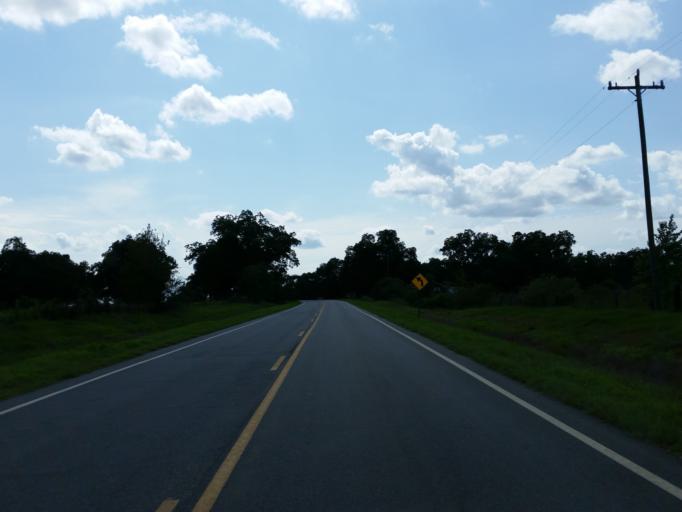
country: US
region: Georgia
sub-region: Turner County
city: Ashburn
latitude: 31.6669
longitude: -83.6158
